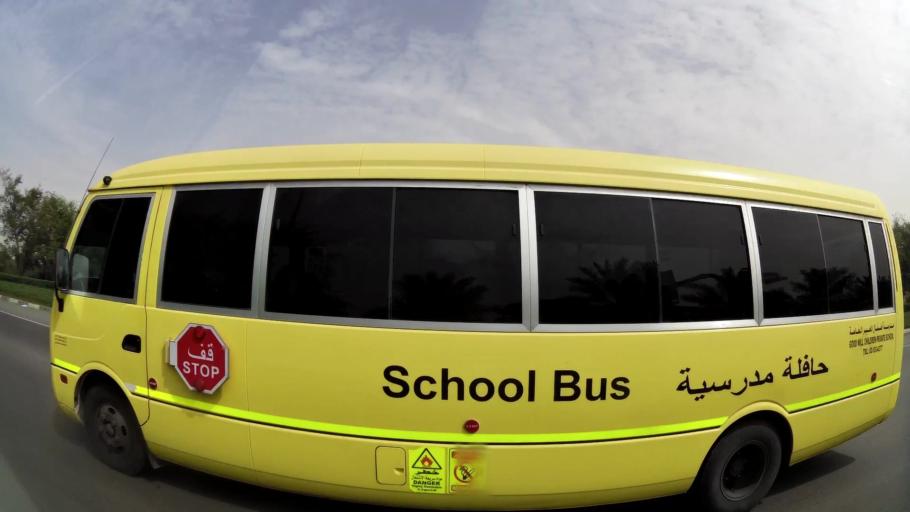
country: AE
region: Abu Dhabi
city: Abu Dhabi
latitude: 24.3440
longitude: 54.5264
